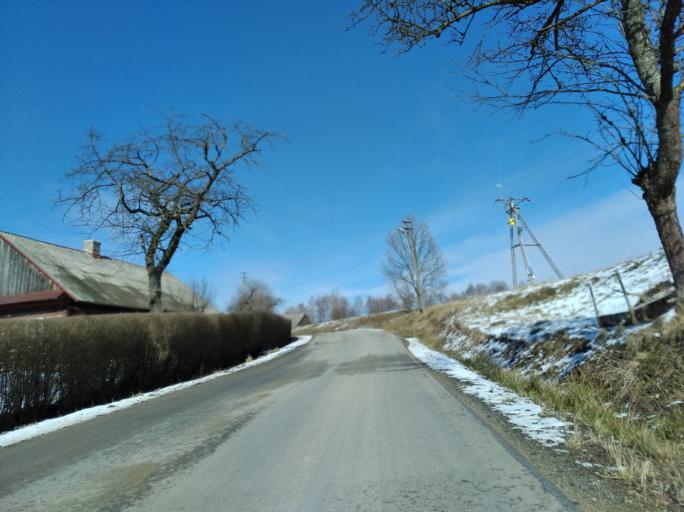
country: PL
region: Subcarpathian Voivodeship
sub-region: Powiat brzozowski
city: Jablonica Polska
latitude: 49.7232
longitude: 21.8796
